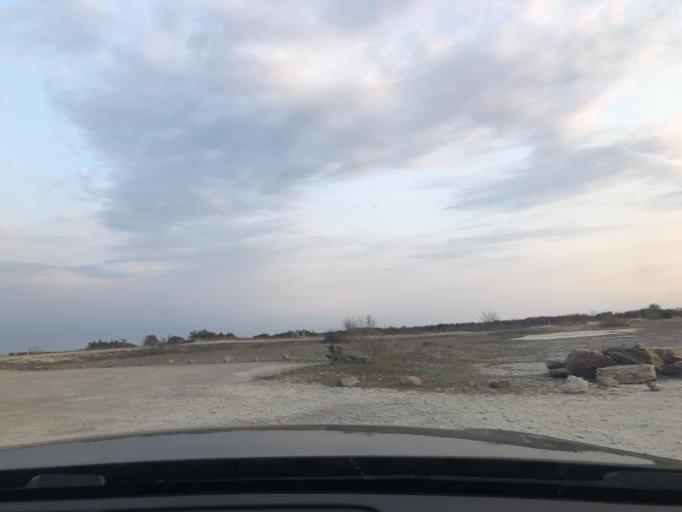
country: SE
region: Kalmar
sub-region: Borgholms Kommun
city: Borgholm
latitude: 57.2227
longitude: 16.9515
